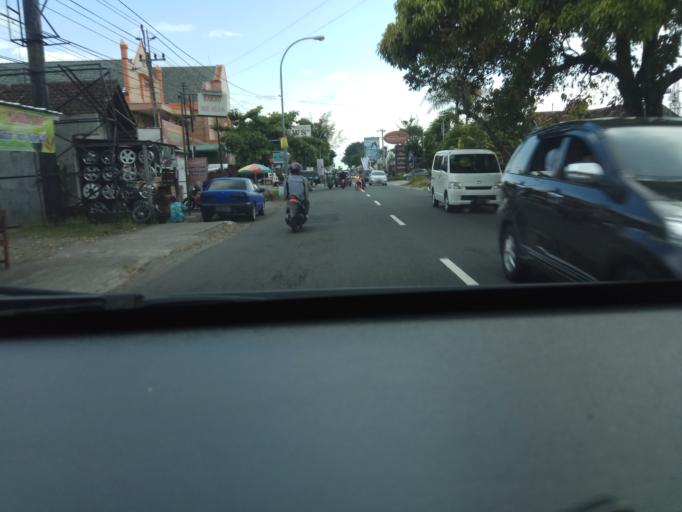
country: ID
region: Daerah Istimewa Yogyakarta
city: Melati
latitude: -7.7122
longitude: 110.4082
